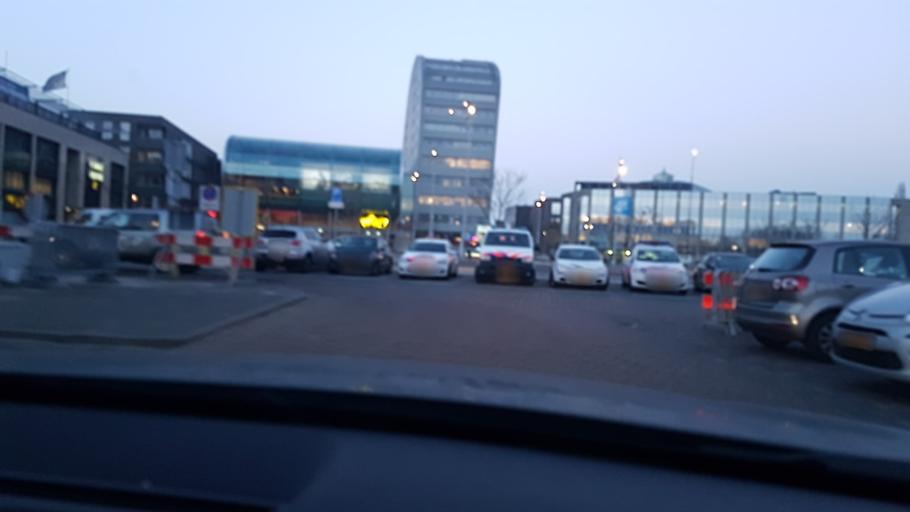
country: NL
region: North Brabant
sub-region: Gemeente Breda
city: Breda
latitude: 51.5883
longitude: 4.7851
